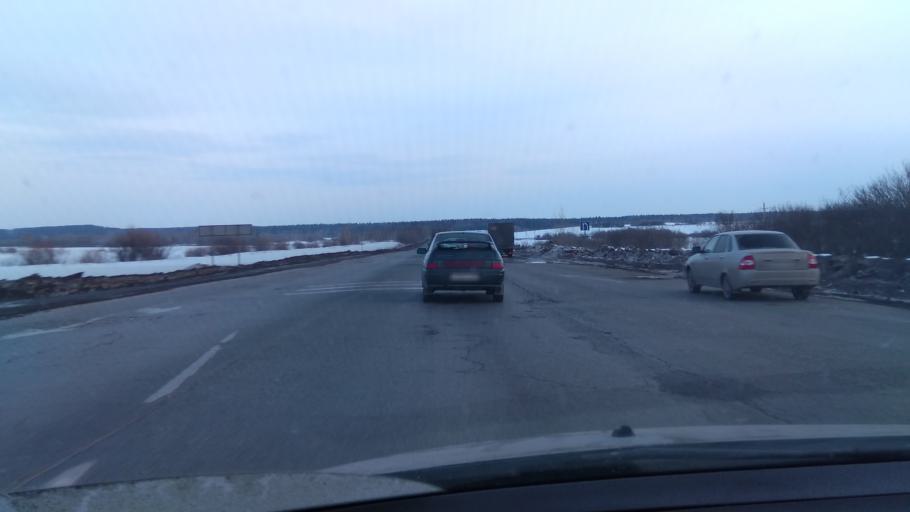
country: RU
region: Perm
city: Kukushtan
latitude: 57.5038
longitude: 56.6516
